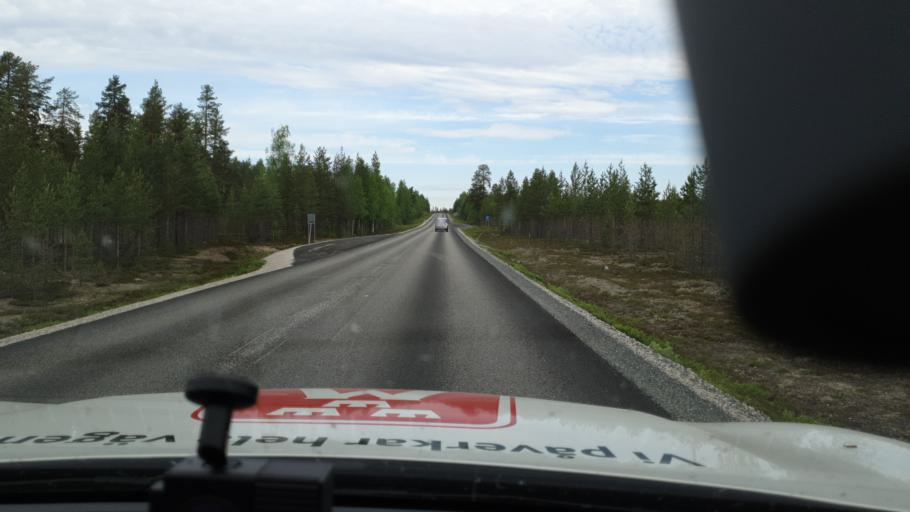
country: SE
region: Vaesterbotten
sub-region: Mala Kommun
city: Mala
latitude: 64.9612
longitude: 18.5871
